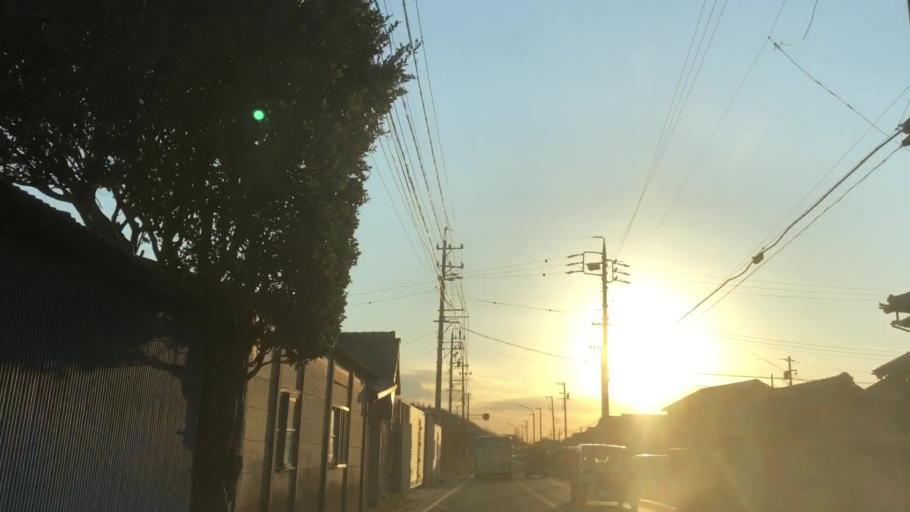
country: JP
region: Aichi
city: Tahara
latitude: 34.6427
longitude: 137.1411
